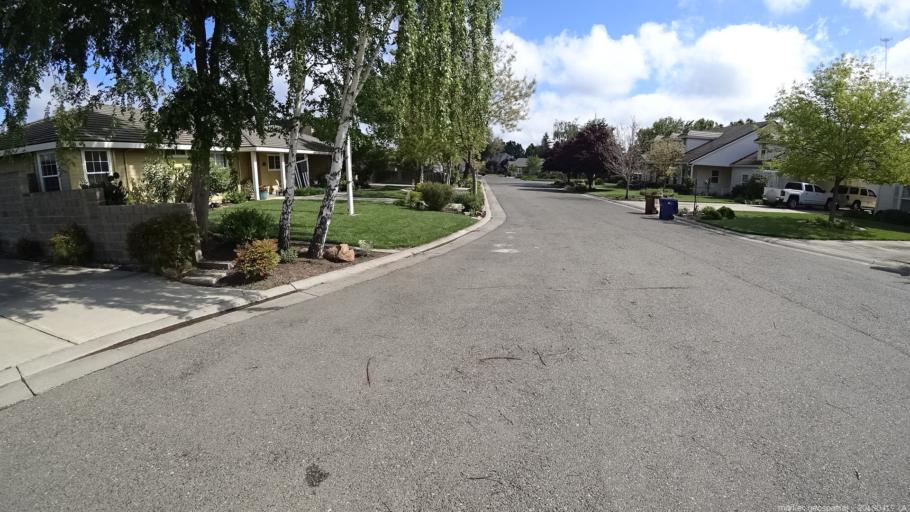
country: US
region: California
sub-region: Sacramento County
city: Walnut Grove
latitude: 38.2453
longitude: -121.5183
